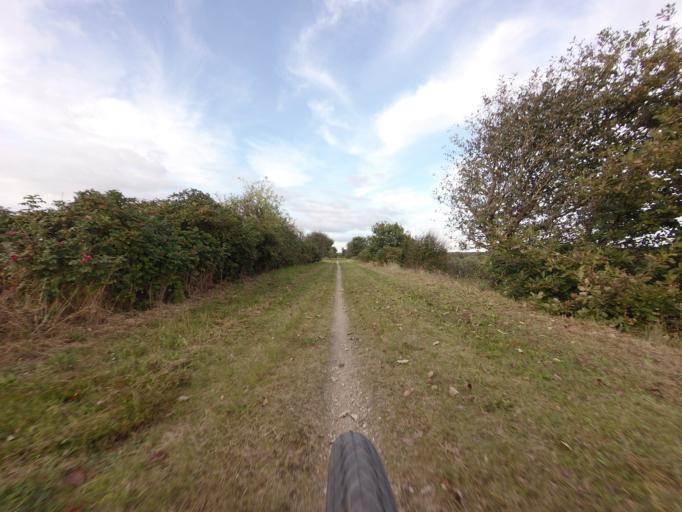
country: DK
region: Central Jutland
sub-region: Ikast-Brande Kommune
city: Brande
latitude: 55.8929
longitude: 9.0678
